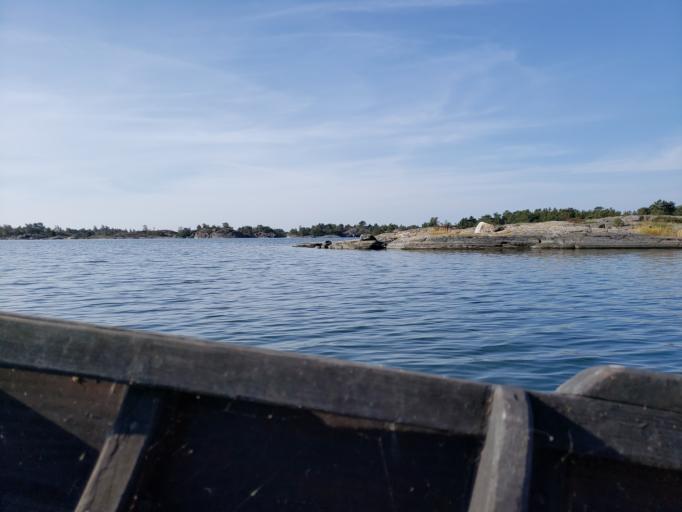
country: FI
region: Varsinais-Suomi
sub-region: Aboland-Turunmaa
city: Dragsfjaerd
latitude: 59.8570
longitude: 22.2107
